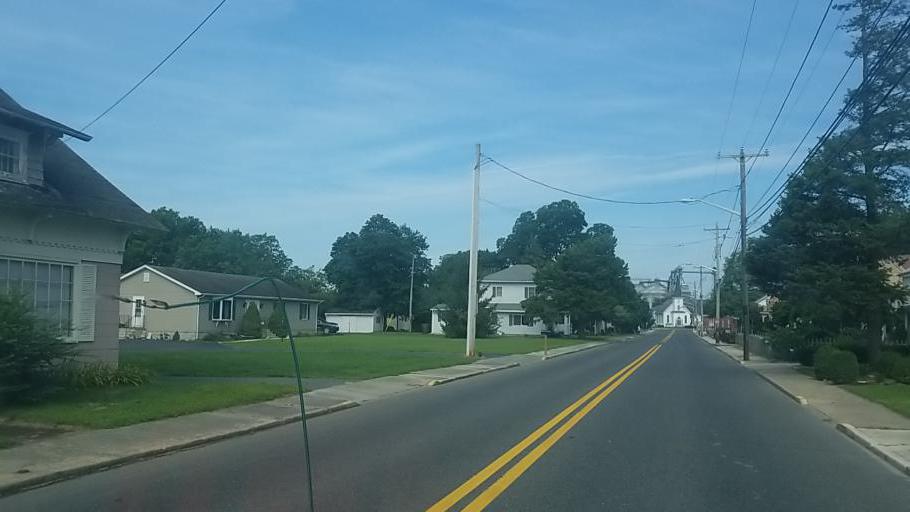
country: US
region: Delaware
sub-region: Sussex County
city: Selbyville
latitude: 38.5167
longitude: -75.2325
